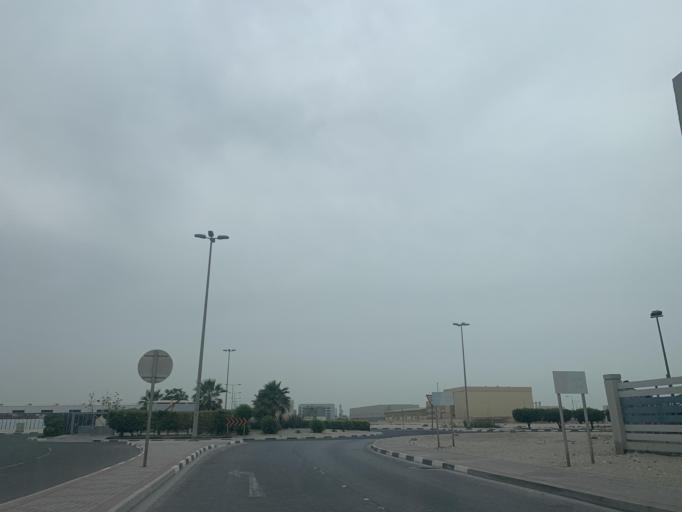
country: BH
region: Muharraq
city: Al Hadd
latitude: 26.2134
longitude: 50.6801
